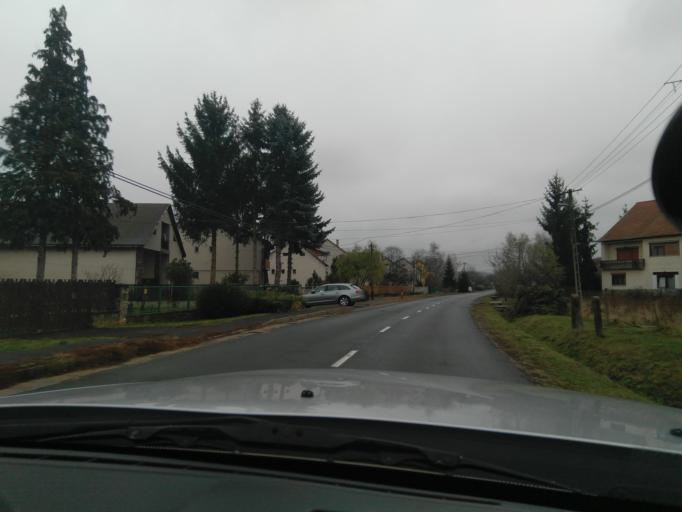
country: HU
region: Nograd
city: Matraterenye
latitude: 48.0394
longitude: 19.9405
